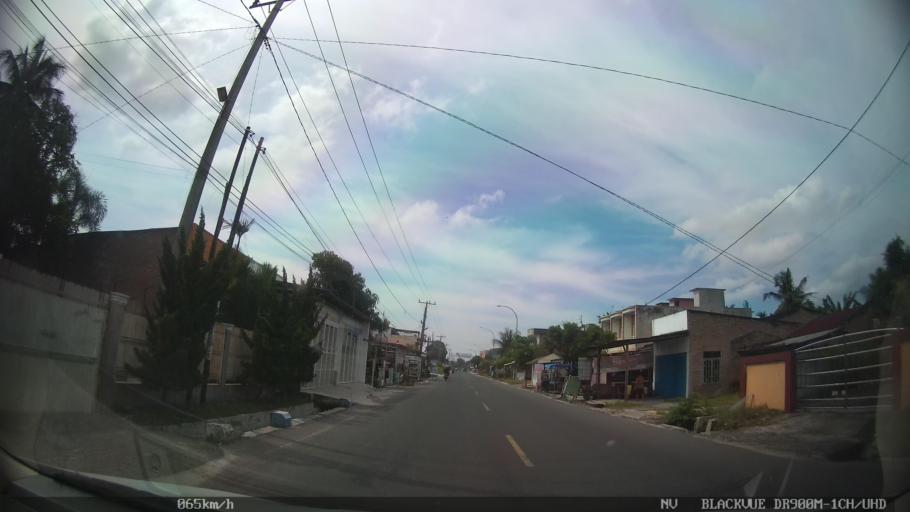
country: ID
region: North Sumatra
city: Percut
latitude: 3.5842
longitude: 98.8616
